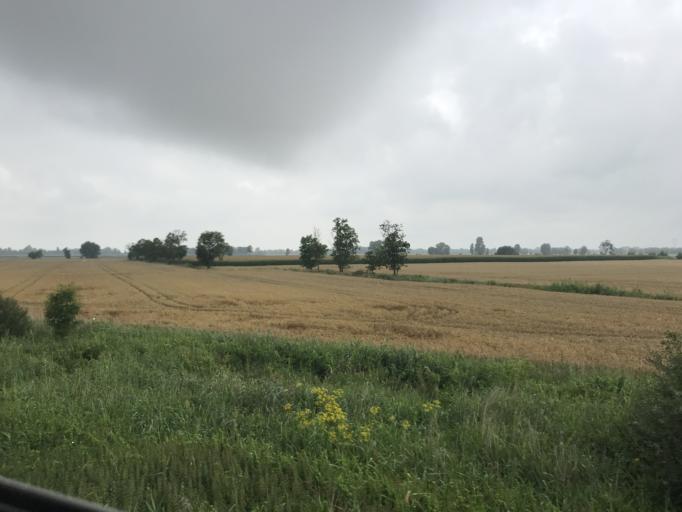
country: PL
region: Warmian-Masurian Voivodeship
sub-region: Powiat elblaski
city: Elblag
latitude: 54.1206
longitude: 19.3578
